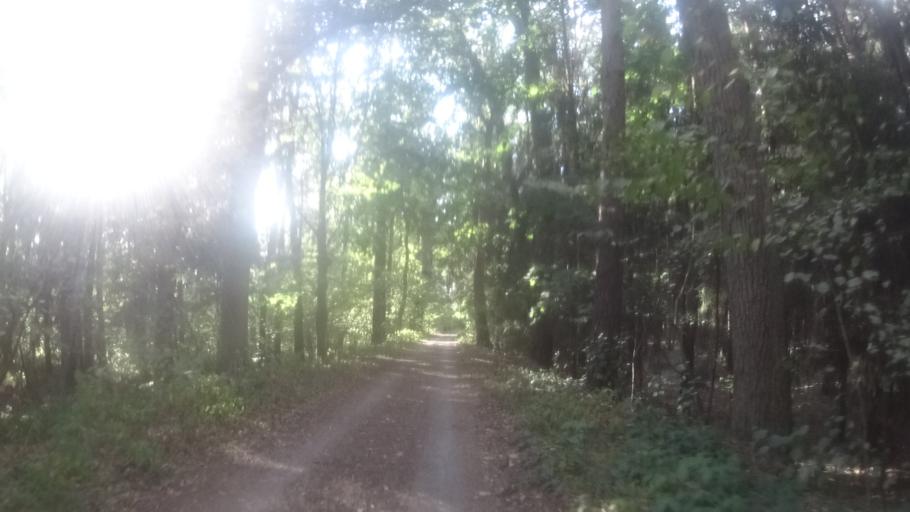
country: CZ
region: Kralovehradecky
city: Trebechovice pod Orebem
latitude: 50.1852
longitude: 16.0147
